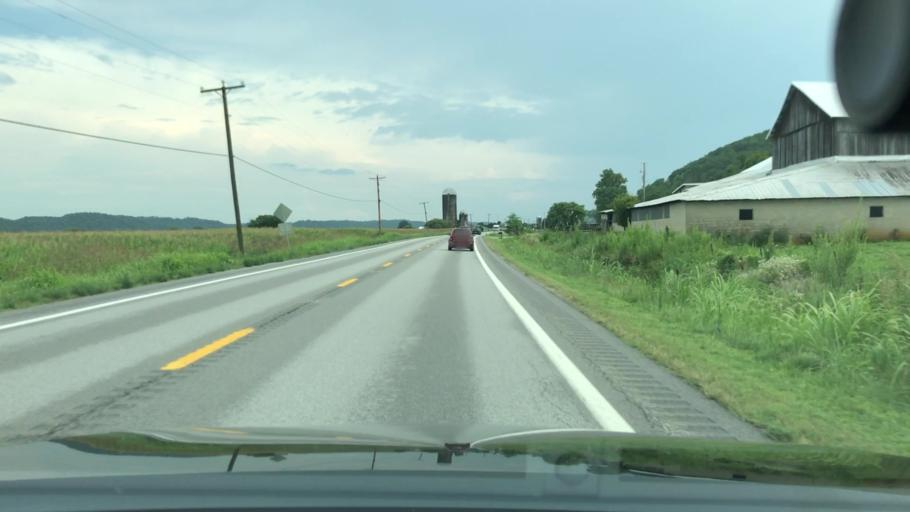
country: US
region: West Virginia
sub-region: Putnam County
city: Buffalo
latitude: 38.7385
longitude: -81.9764
